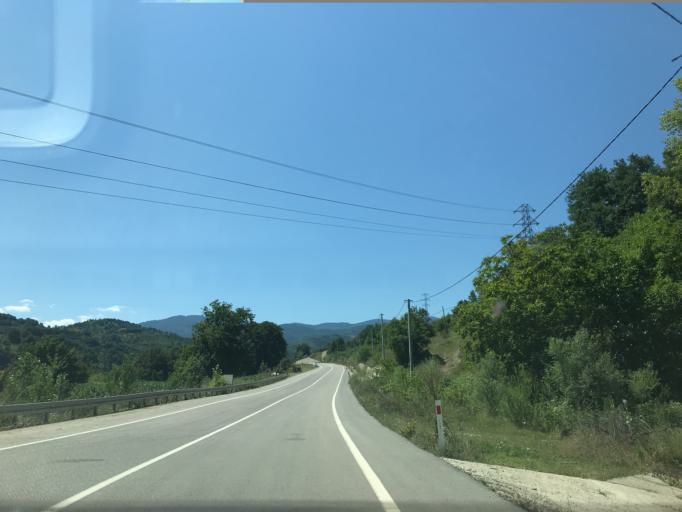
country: TR
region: Bursa
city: Tahtakopru
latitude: 39.9783
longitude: 29.6045
